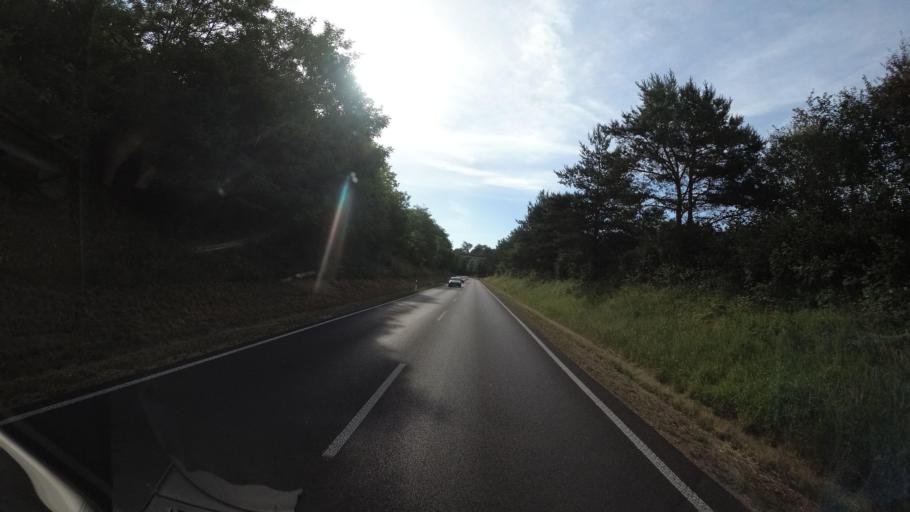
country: DE
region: Baden-Wuerttemberg
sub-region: Freiburg Region
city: Weil am Rhein
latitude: 47.5878
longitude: 7.6297
